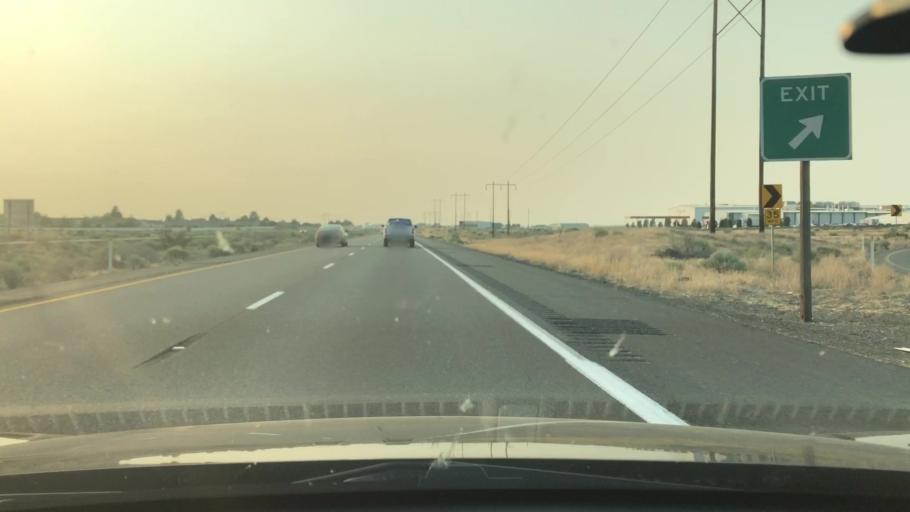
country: US
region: Washington
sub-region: Franklin County
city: Pasco
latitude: 46.2403
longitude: -119.0576
